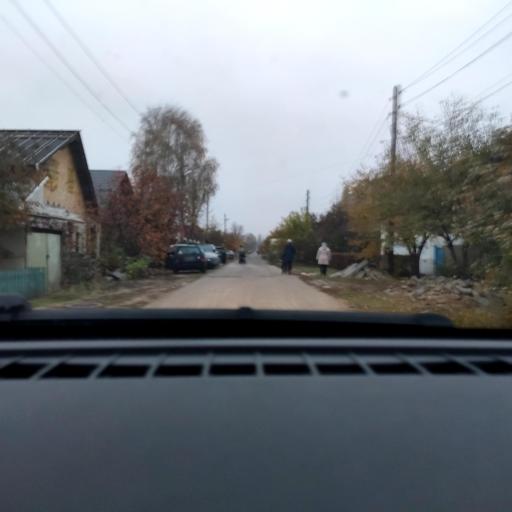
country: RU
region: Voronezj
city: Maslovka
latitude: 51.6318
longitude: 39.2820
